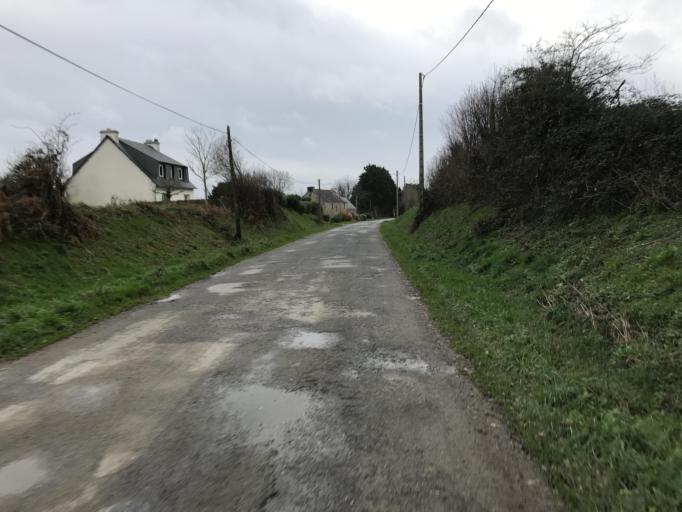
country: FR
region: Brittany
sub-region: Departement du Finistere
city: Daoulas
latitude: 48.3588
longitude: -4.2765
